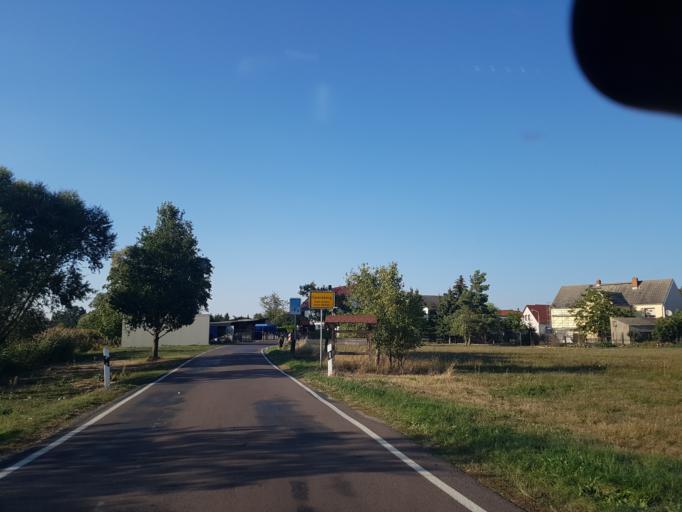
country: DE
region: Saxony
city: Nauwalde
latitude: 51.4168
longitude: 13.3908
